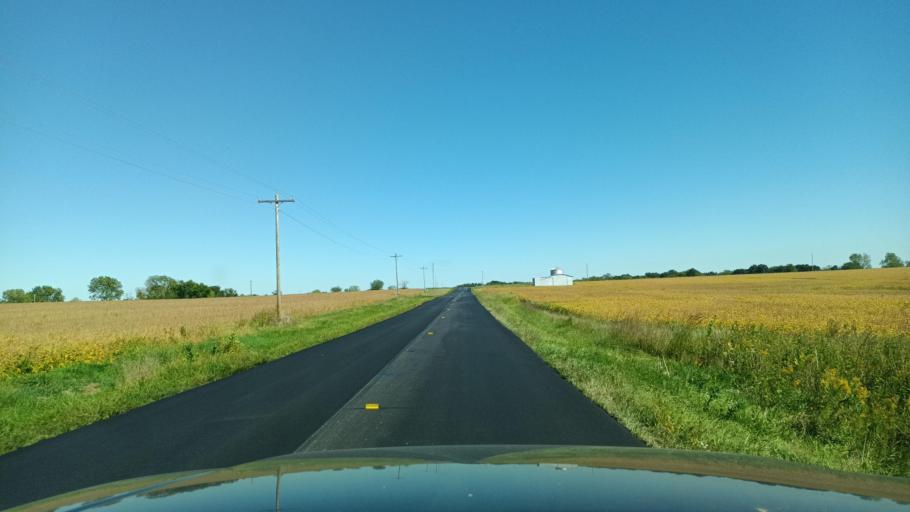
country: US
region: Missouri
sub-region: Macon County
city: La Plata
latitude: 39.9277
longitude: -92.5546
